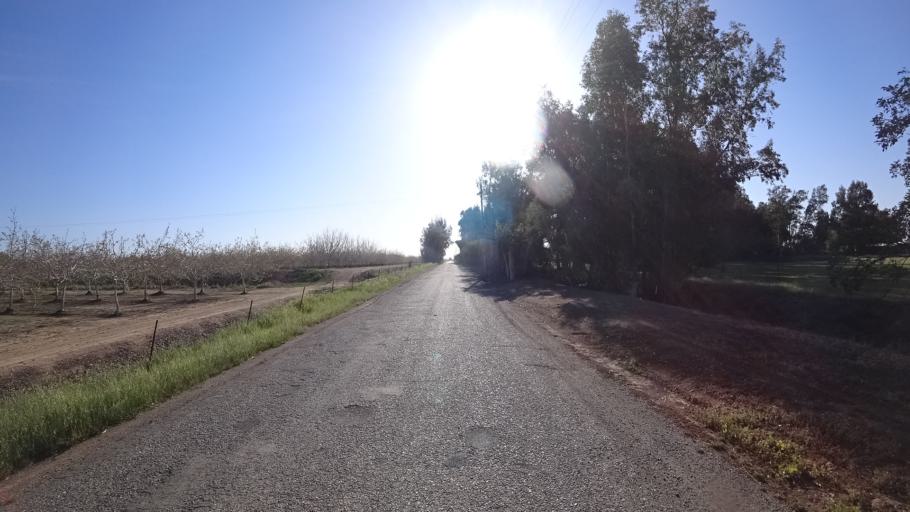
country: US
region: California
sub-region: Glenn County
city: Orland
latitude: 39.6818
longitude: -122.1541
